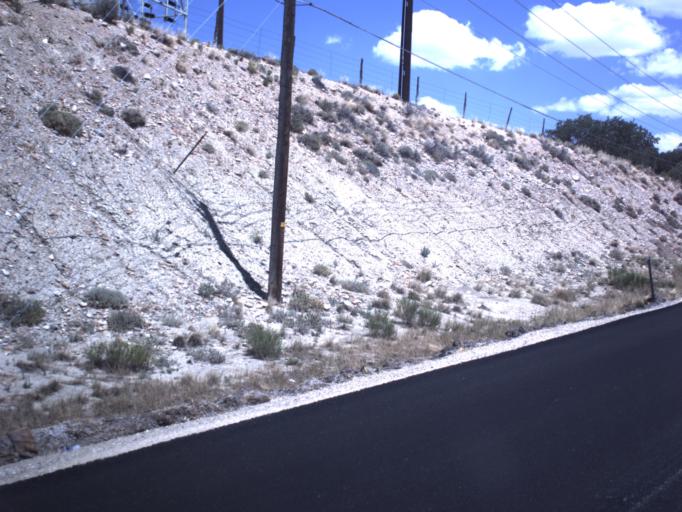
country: US
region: Utah
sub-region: Emery County
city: Orangeville
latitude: 39.2282
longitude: -111.0401
